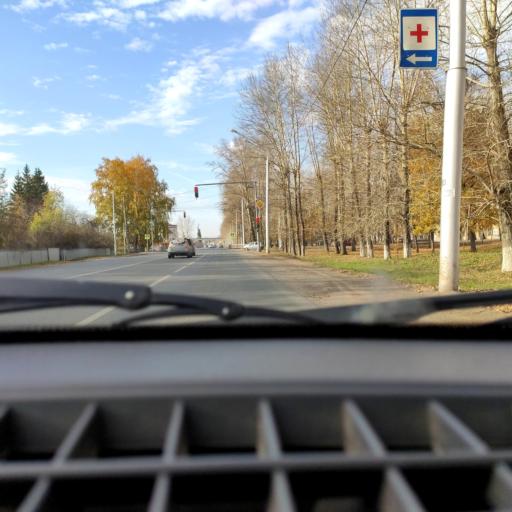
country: RU
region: Bashkortostan
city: Mikhaylovka
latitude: 54.7012
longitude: 55.8406
